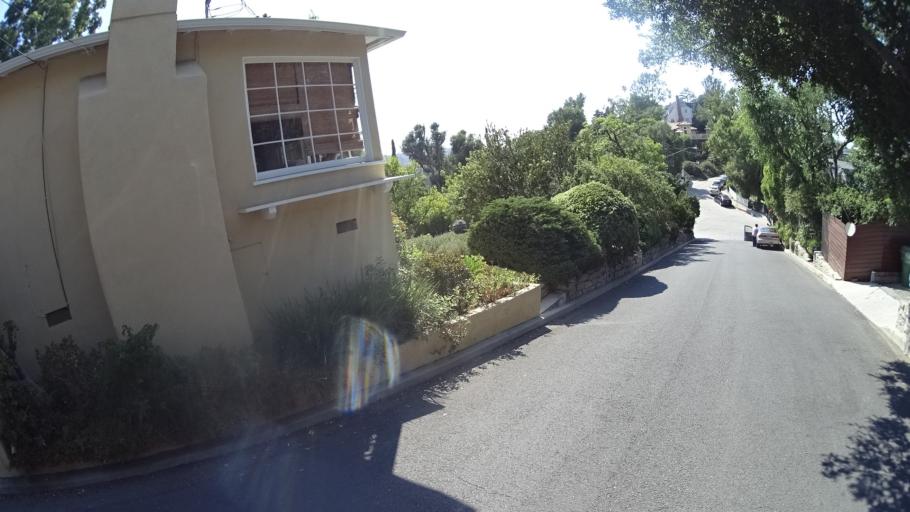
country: US
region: California
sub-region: Los Angeles County
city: Universal City
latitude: 34.1379
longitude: -118.3851
